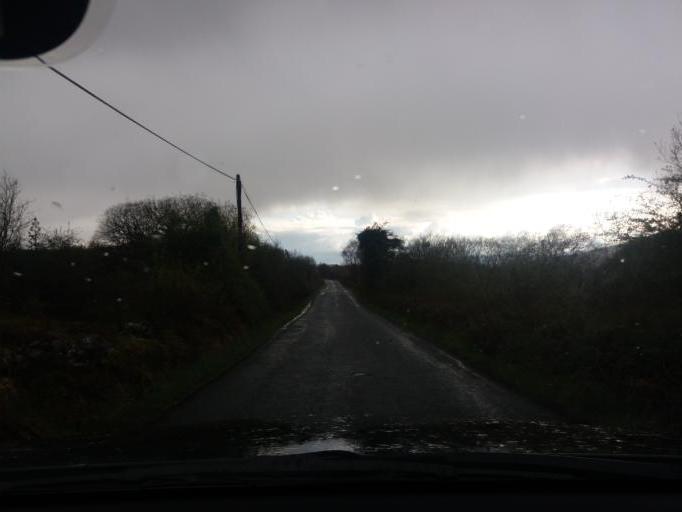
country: IE
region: Connaught
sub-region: County Leitrim
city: Manorhamilton
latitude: 54.2588
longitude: -7.9258
